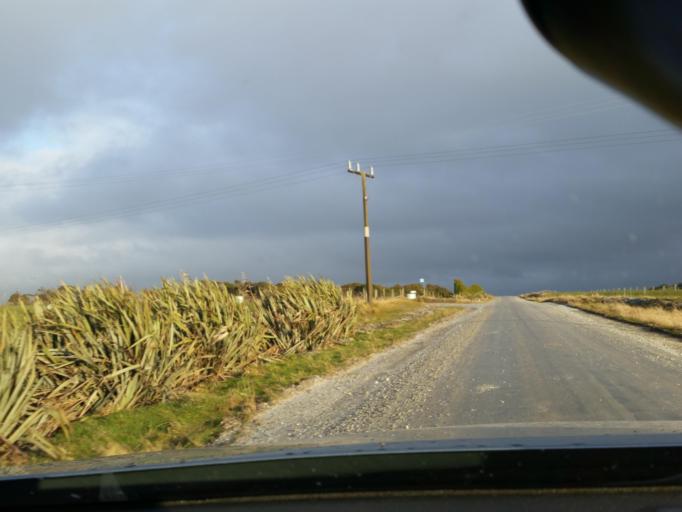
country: NZ
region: Southland
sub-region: Invercargill City
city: Invercargill
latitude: -46.4339
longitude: 168.5062
